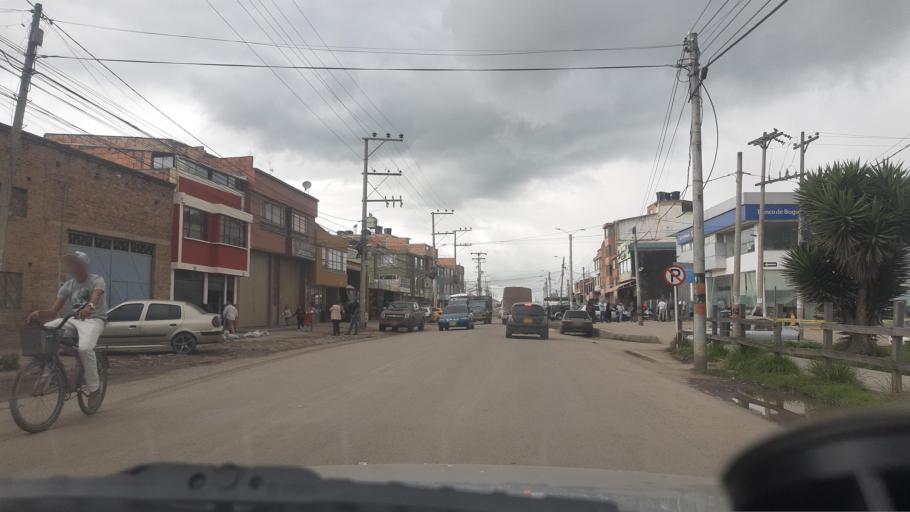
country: CO
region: Cundinamarca
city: Ubate
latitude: 5.3116
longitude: -73.8113
